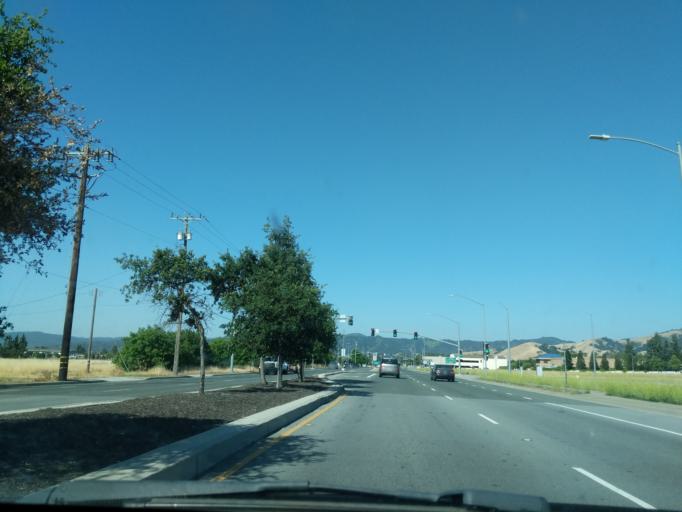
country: US
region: California
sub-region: Santa Clara County
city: Morgan Hill
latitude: 37.1181
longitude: -121.6295
